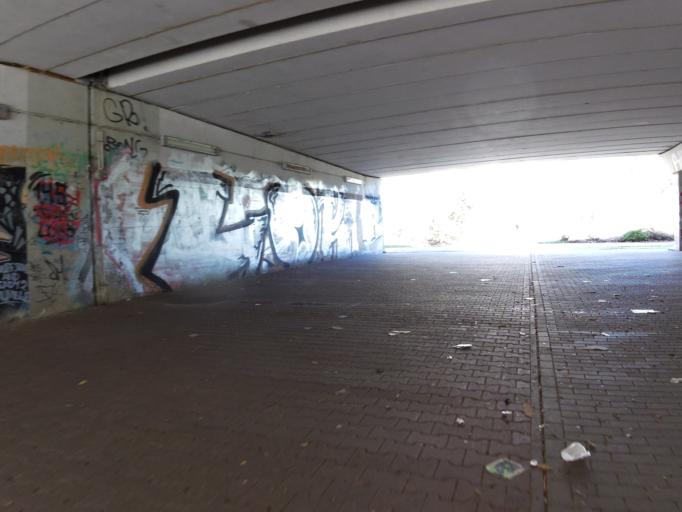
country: DE
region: Saxony
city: Markranstadt
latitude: 51.3200
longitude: 12.2926
